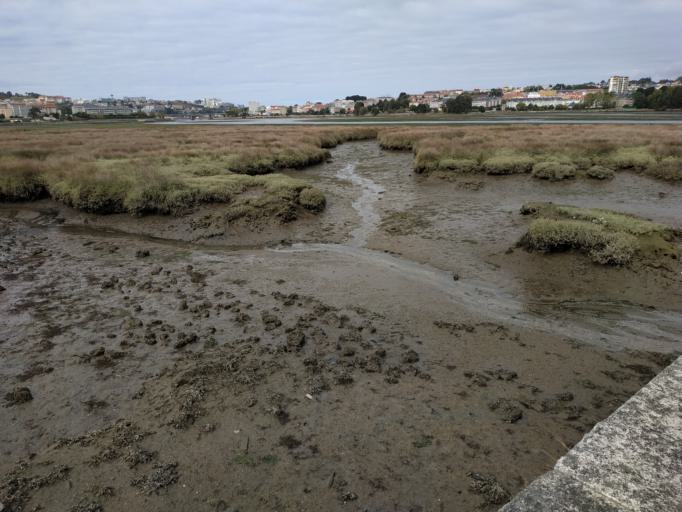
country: ES
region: Galicia
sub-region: Provincia da Coruna
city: Culleredo
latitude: 43.3215
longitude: -8.3728
